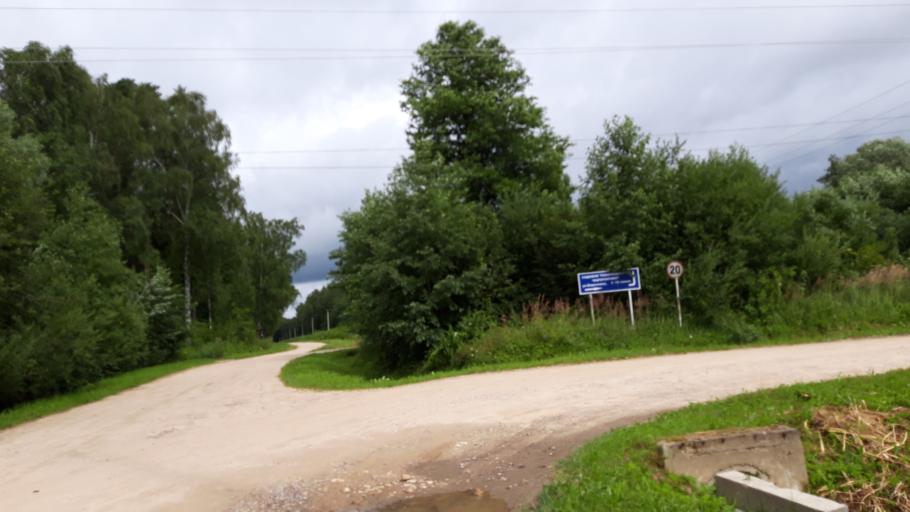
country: RU
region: Tverskaya
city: Konakovo
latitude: 56.6820
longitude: 36.7124
